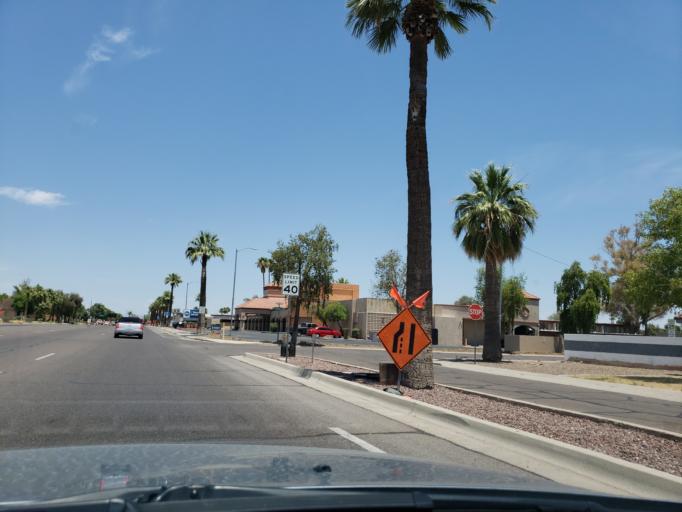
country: US
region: Arizona
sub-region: Maricopa County
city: Goodyear
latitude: 33.4459
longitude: -112.3582
